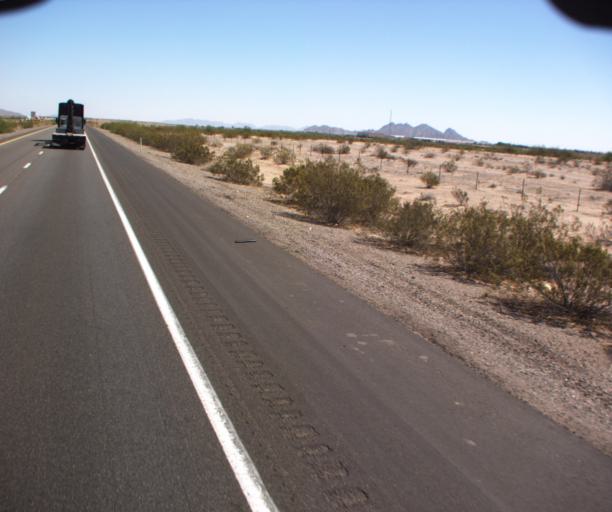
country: US
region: Arizona
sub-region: Yuma County
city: Wellton
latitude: 32.6668
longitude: -114.1205
